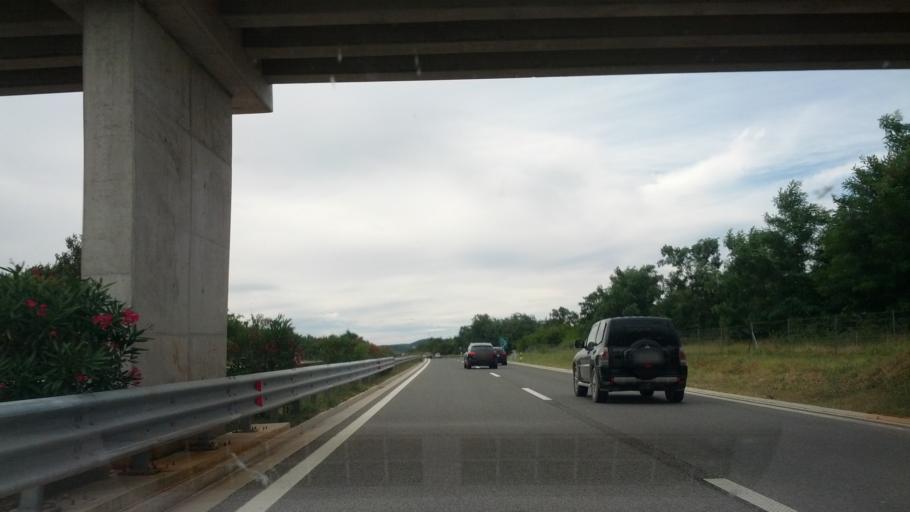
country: HR
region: Istarska
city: Vrsar
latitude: 45.1907
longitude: 13.7311
